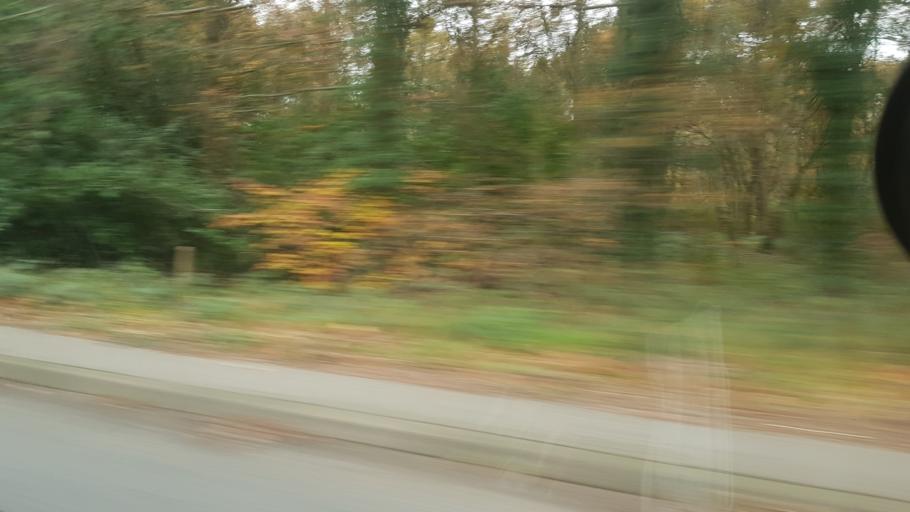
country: GB
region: England
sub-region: Hampshire
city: Aldershot
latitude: 51.2649
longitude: -0.7641
